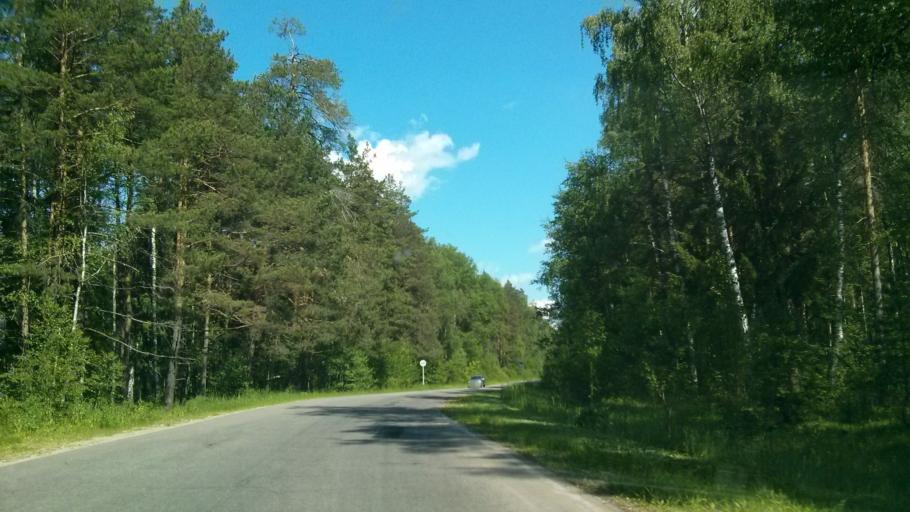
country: RU
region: Vladimir
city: Melenki
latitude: 55.3335
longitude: 41.6762
